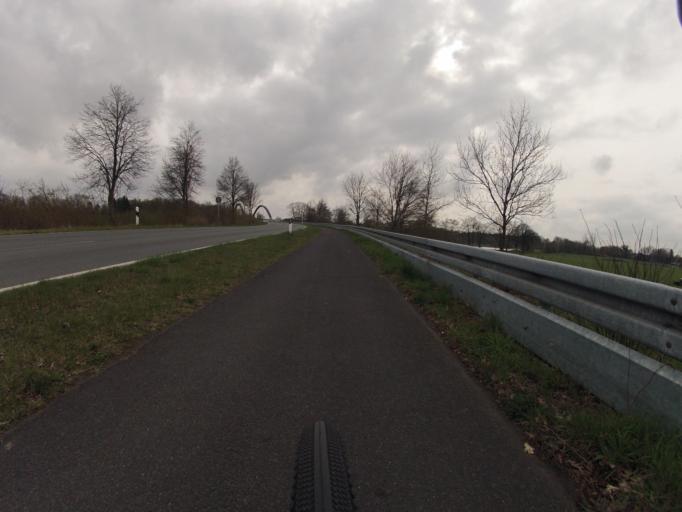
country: DE
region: North Rhine-Westphalia
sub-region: Regierungsbezirk Munster
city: Recke
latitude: 52.3572
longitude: 7.7162
